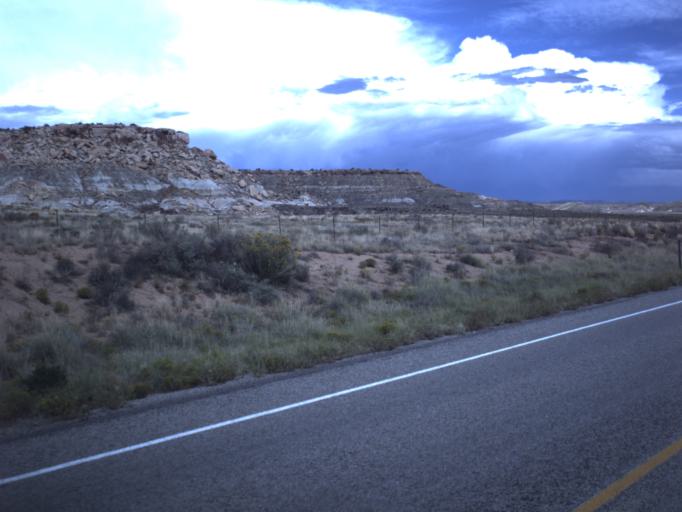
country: US
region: Colorado
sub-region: Montezuma County
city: Towaoc
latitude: 37.1603
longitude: -109.0664
